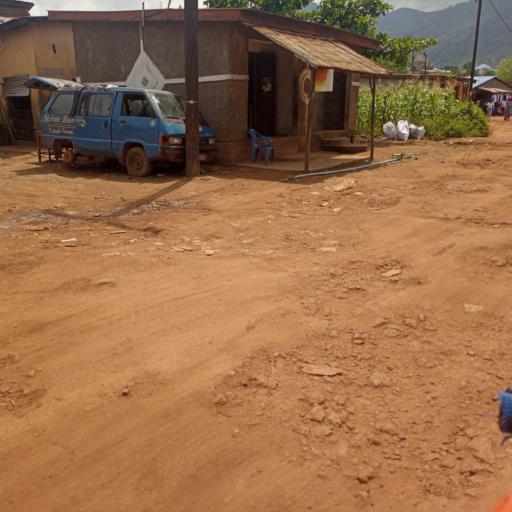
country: SL
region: Western Area
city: Hastings
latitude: 8.3848
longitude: -13.1464
